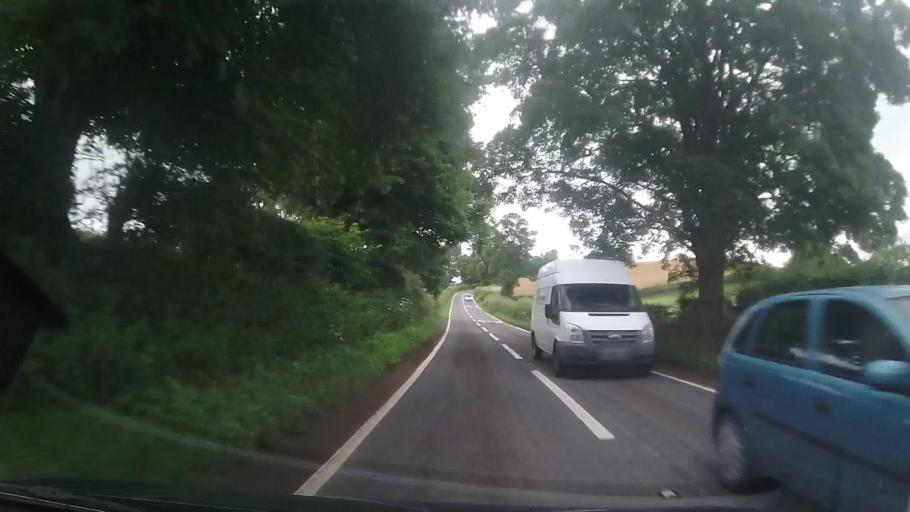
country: GB
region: England
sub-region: Shropshire
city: Petton
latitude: 52.8699
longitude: -2.8555
